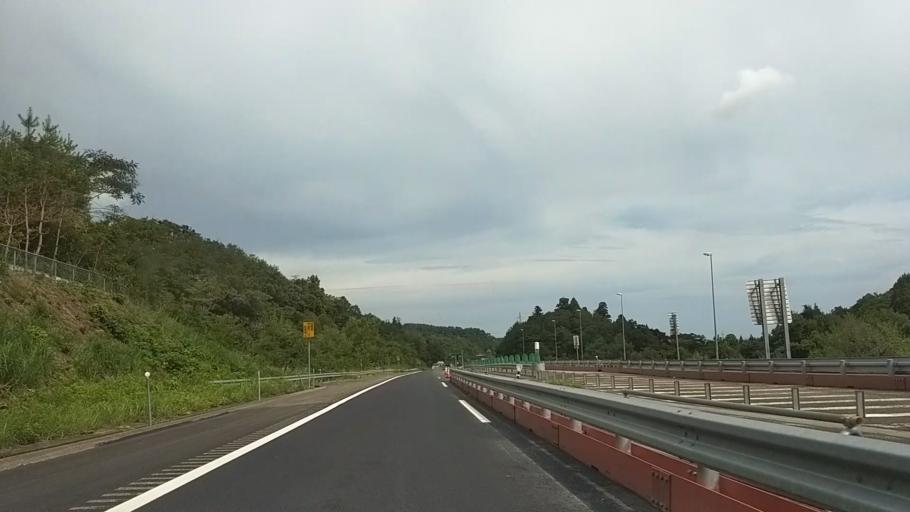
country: JP
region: Niigata
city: Joetsu
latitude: 37.1241
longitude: 138.2127
